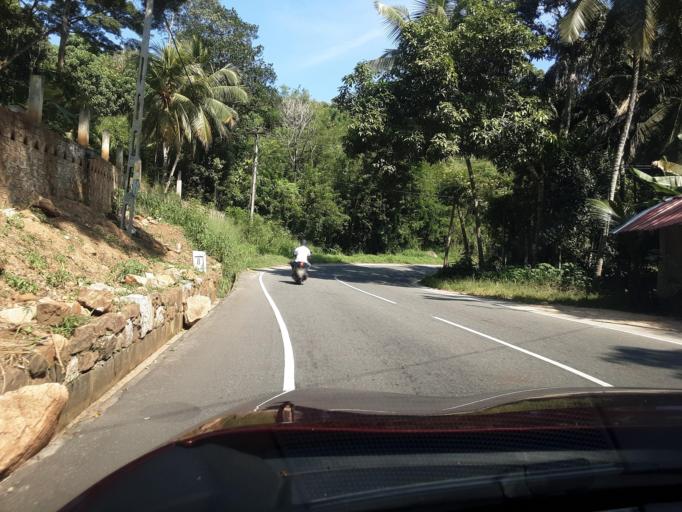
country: LK
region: Uva
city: Badulla
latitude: 7.0386
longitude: 81.0597
